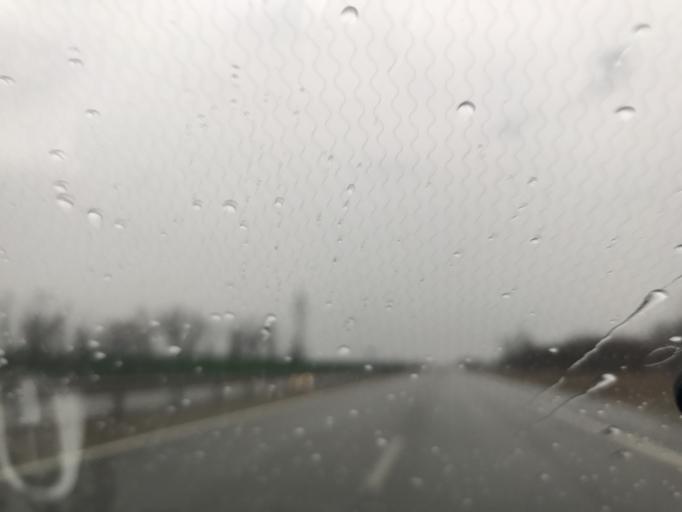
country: RU
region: Krasnodarskiy
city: Krylovskaya
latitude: 46.3103
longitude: 39.8066
